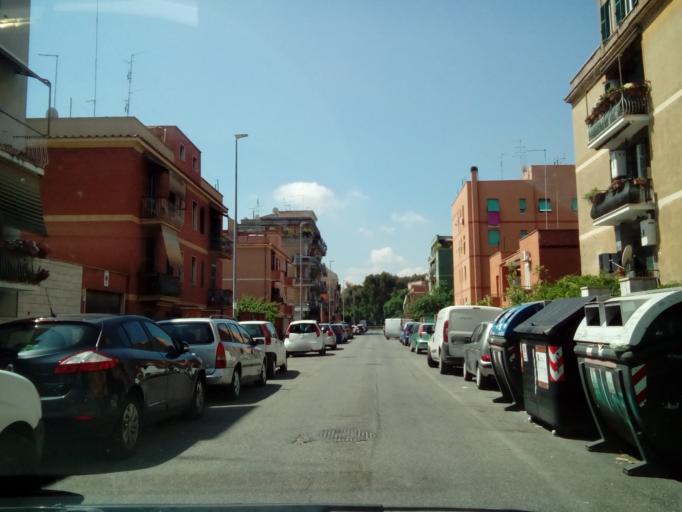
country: IT
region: Latium
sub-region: Citta metropolitana di Roma Capitale
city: Rome
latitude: 41.8761
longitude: 12.5702
